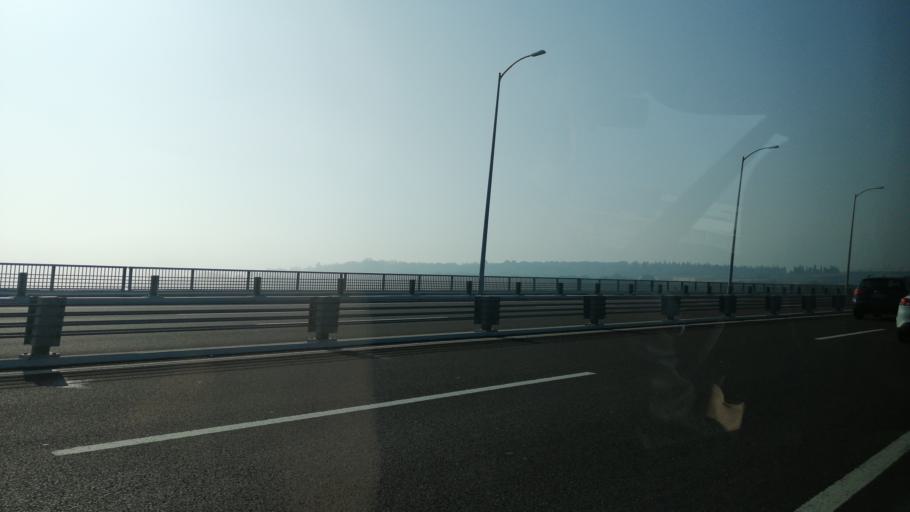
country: TR
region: Yalova
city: Altinova
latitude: 40.7330
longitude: 29.5097
